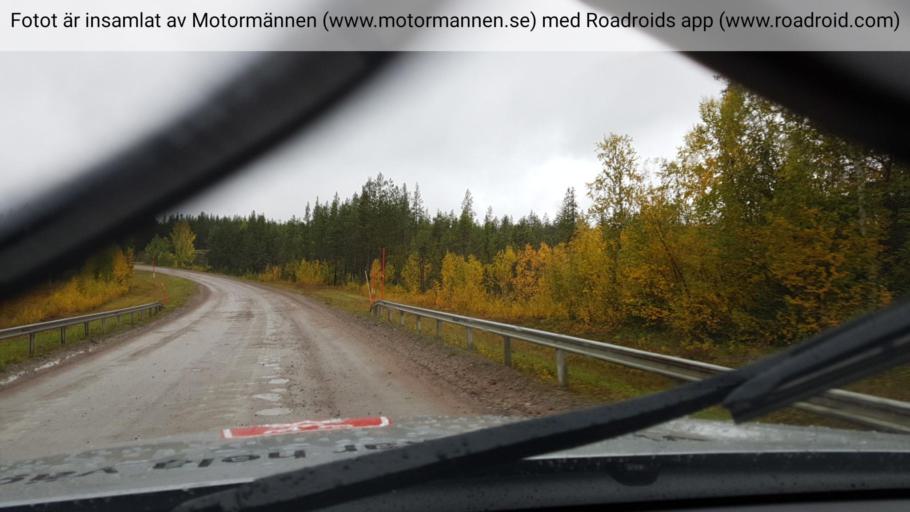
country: SE
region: Norrbotten
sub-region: Alvsbyns Kommun
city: AElvsbyn
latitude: 66.2761
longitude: 21.0922
